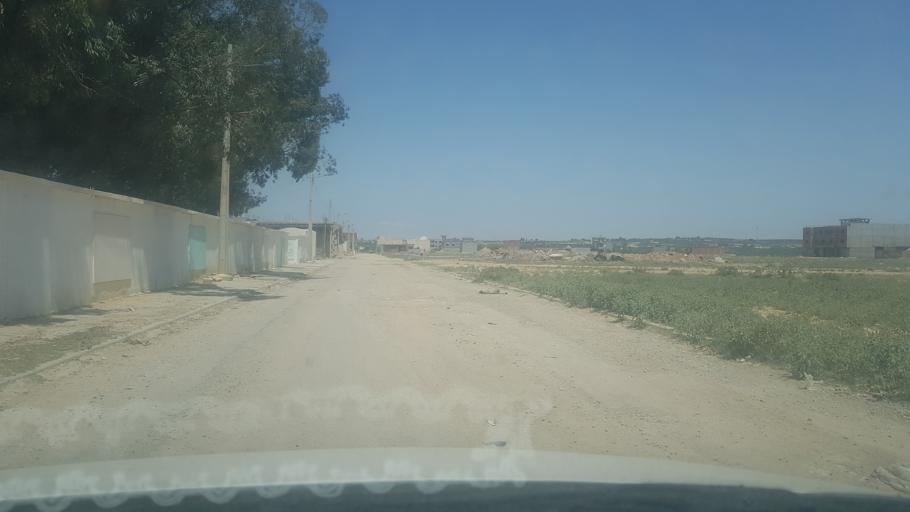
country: TN
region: Al Qayrawan
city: Kairouan
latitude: 35.6177
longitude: 9.9304
